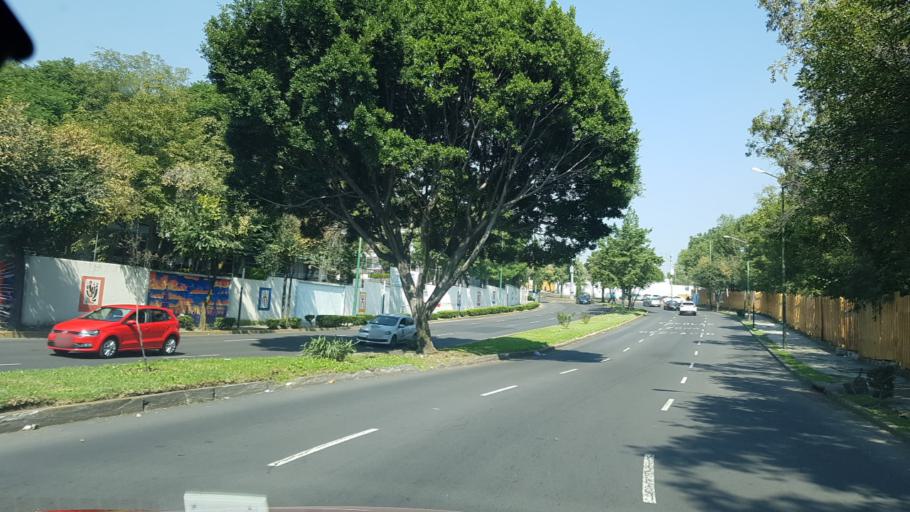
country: MX
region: Mexico City
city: Alvaro Obregon
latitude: 19.3536
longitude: -99.2132
